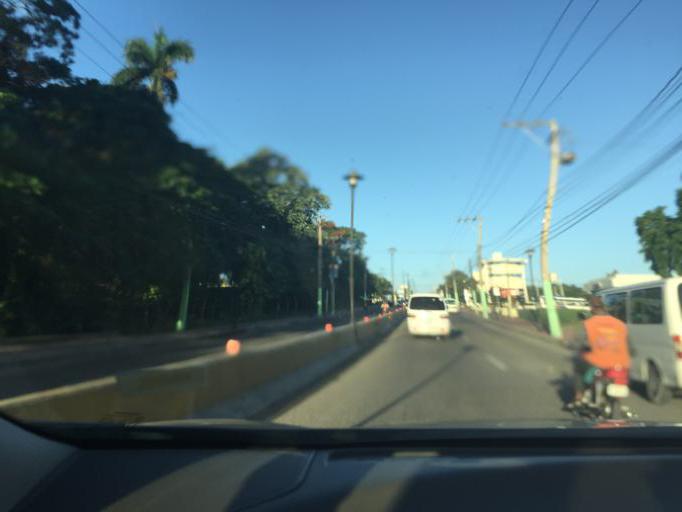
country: DO
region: Puerto Plata
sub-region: Puerto Plata
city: Puerto Plata
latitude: 19.7829
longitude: -70.6747
